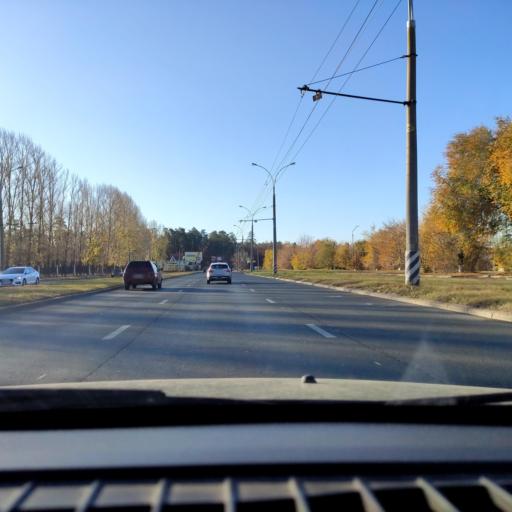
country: RU
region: Samara
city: Tol'yatti
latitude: 53.5011
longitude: 49.2987
